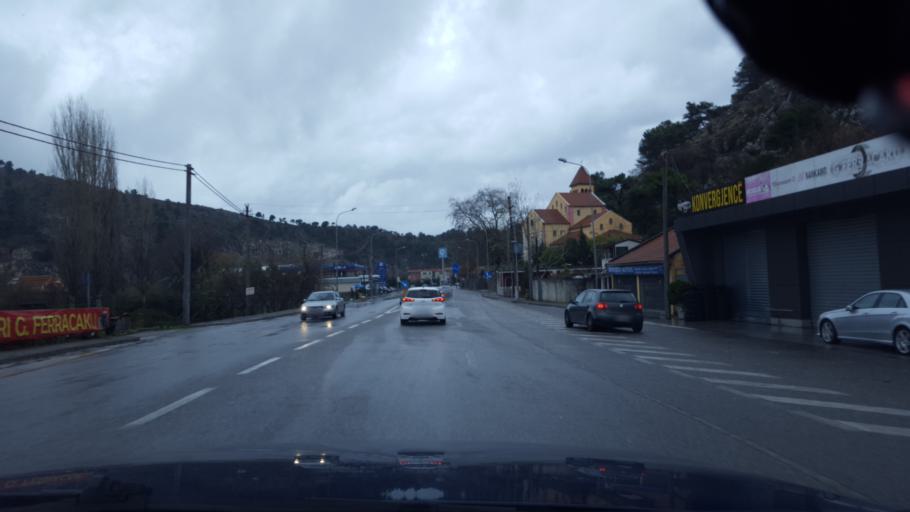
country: AL
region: Shkoder
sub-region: Rrethi i Shkodres
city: Berdica e Madhe
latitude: 42.0429
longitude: 19.4914
